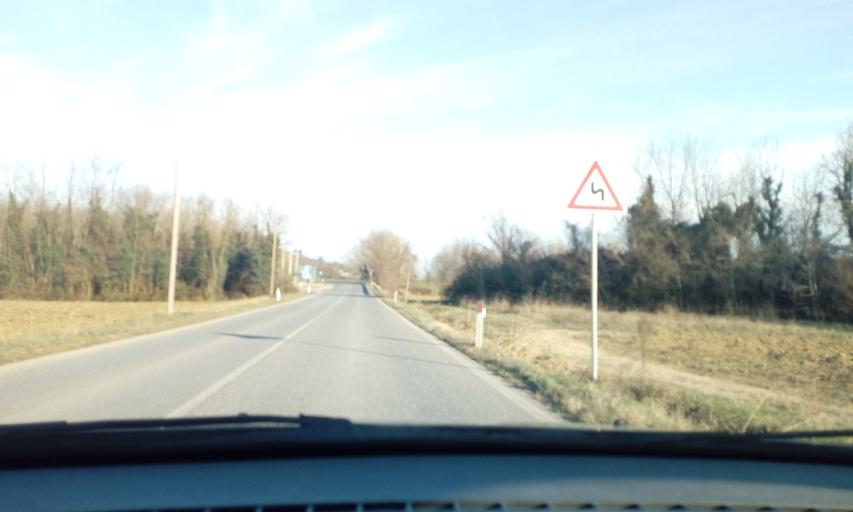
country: IT
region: Friuli Venezia Giulia
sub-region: Provincia di Udine
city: Chiopris
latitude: 45.9164
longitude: 13.4093
